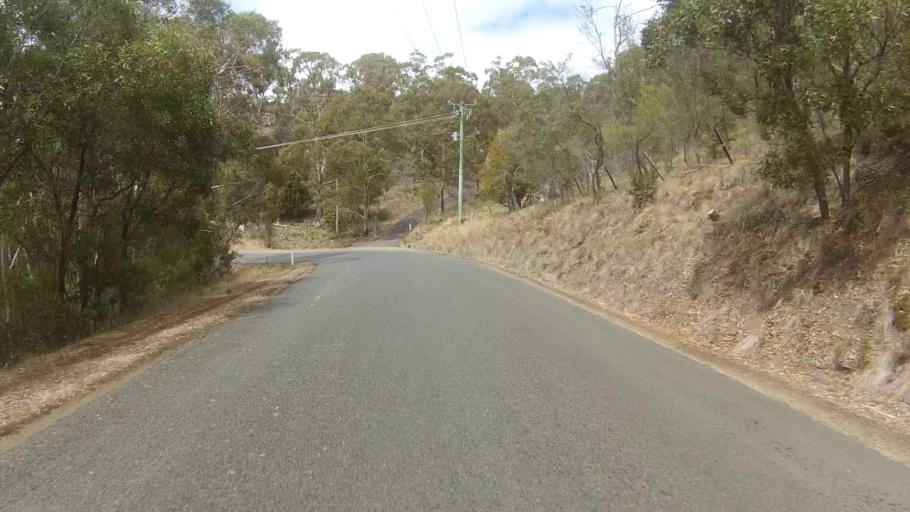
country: AU
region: Tasmania
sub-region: Kingborough
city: Blackmans Bay
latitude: -43.0333
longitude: 147.3303
